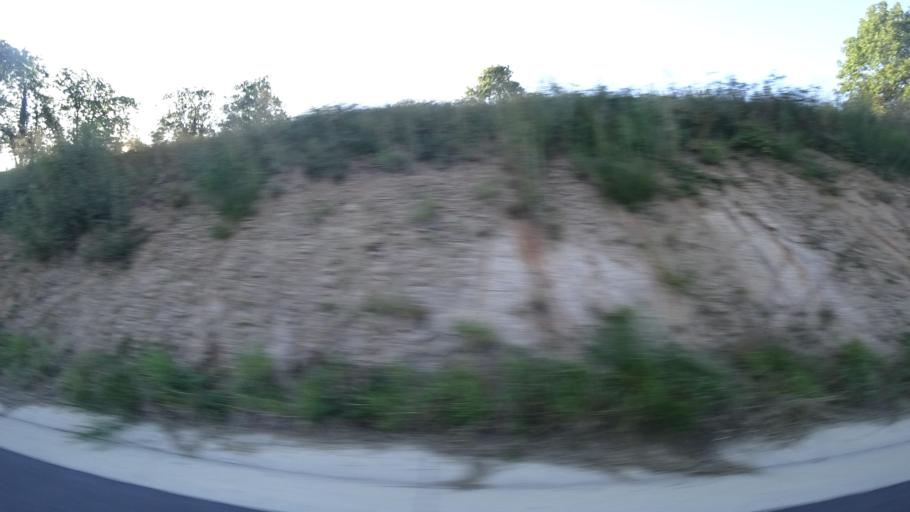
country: FR
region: Midi-Pyrenees
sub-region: Departement de l'Aveyron
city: Luc-la-Primaube
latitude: 44.3188
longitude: 2.5513
